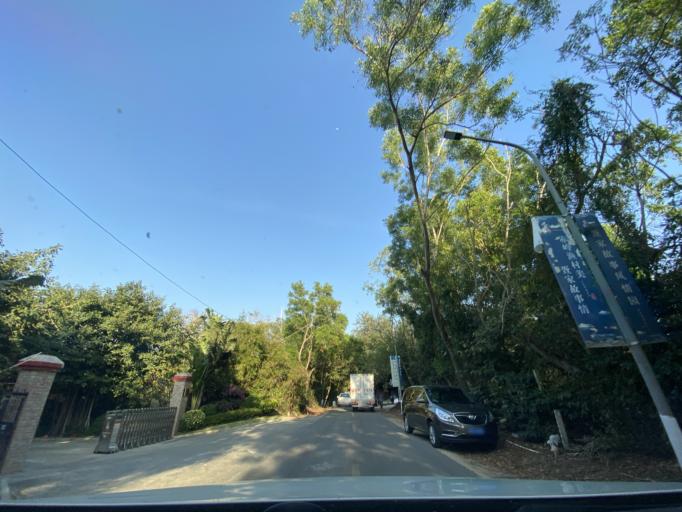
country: CN
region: Hainan
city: Yingzhou
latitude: 18.3880
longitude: 109.8259
